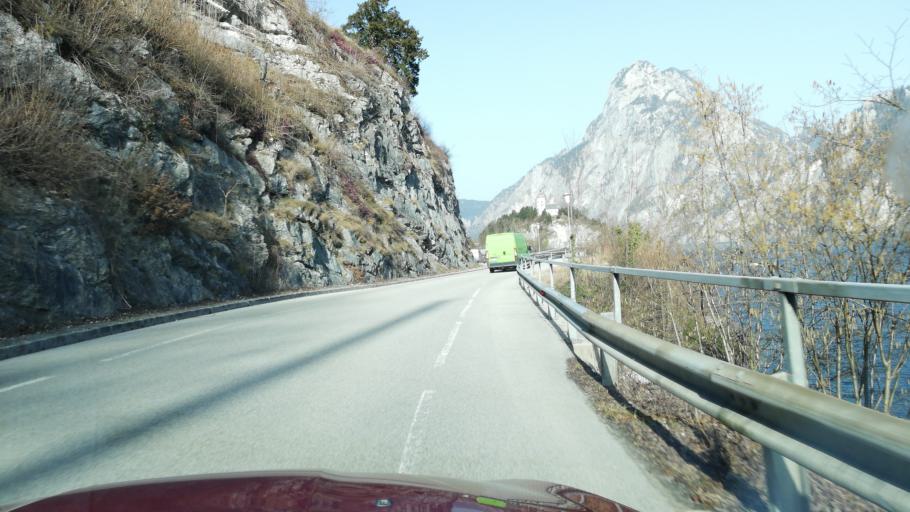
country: AT
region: Upper Austria
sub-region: Politischer Bezirk Gmunden
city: Ebensee
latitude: 47.8403
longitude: 13.7865
